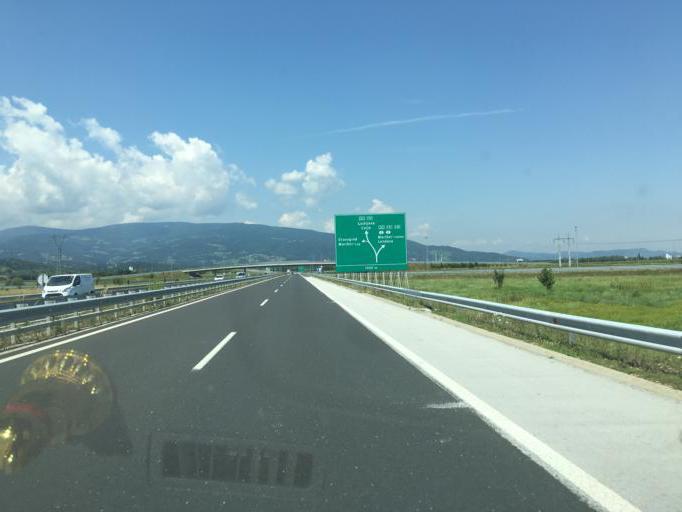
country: SI
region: Hoce-Slivnica
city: Hotinja Vas
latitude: 46.4729
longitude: 15.6784
